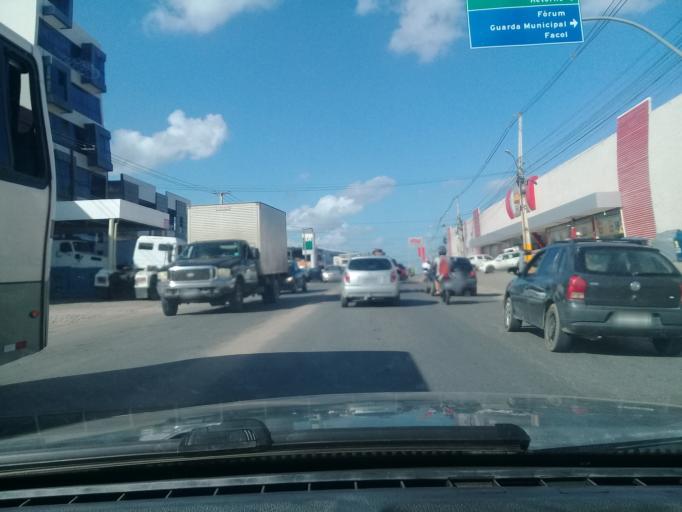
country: BR
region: Pernambuco
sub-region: Vitoria De Santo Antao
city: Vitoria de Santo Antao
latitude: -8.1135
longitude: -35.2942
